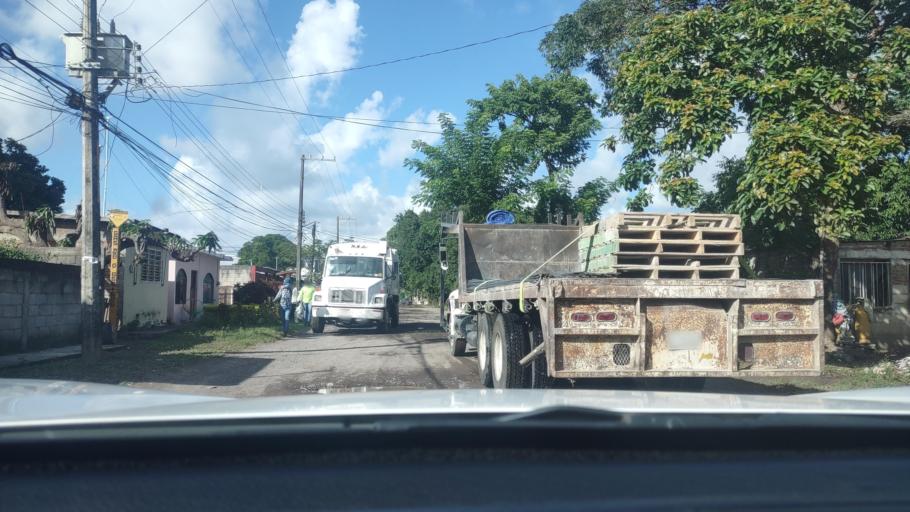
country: MX
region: Veracruz
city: El Tejar
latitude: 19.0697
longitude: -96.1589
